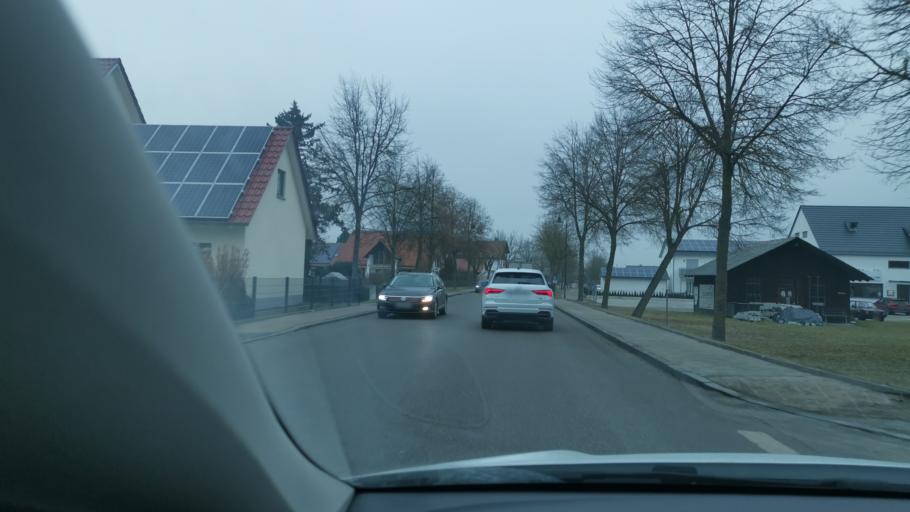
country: DE
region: Bavaria
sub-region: Swabia
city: Thierhaupten
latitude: 48.5684
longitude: 10.9072
